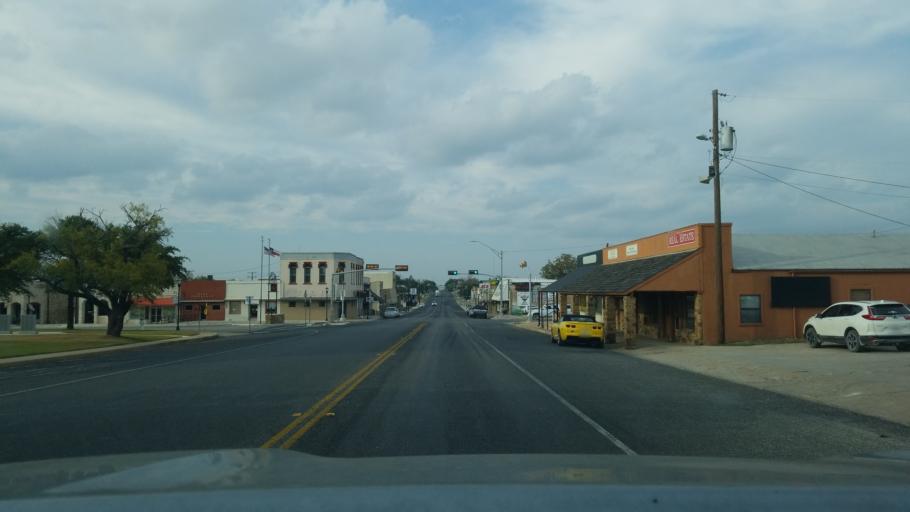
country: US
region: Texas
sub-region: Mills County
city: Goldthwaite
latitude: 31.4498
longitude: -98.5689
